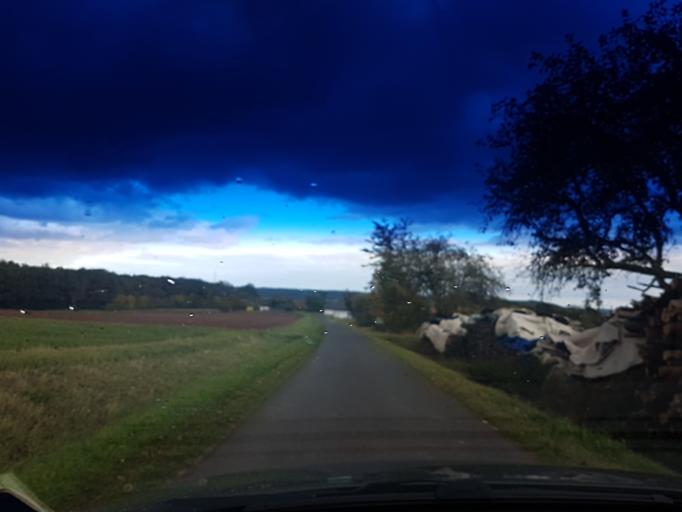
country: DE
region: Bavaria
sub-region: Regierungsbezirk Mittelfranken
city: Burghaslach
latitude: 49.7411
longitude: 10.5940
